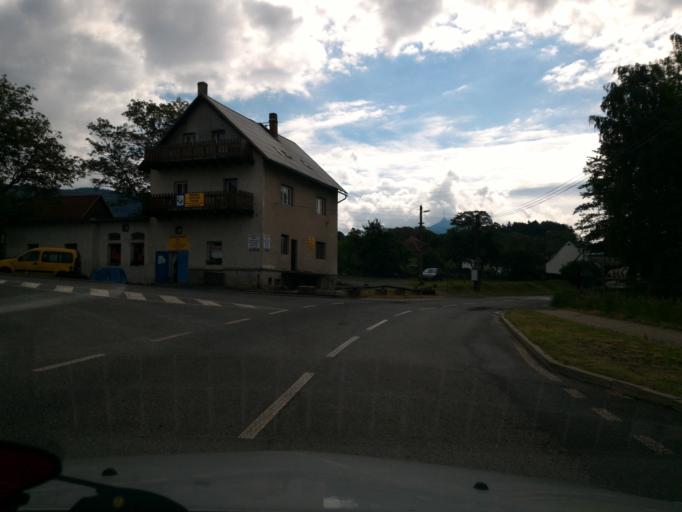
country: CZ
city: Osecna
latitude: 50.7390
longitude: 14.9130
